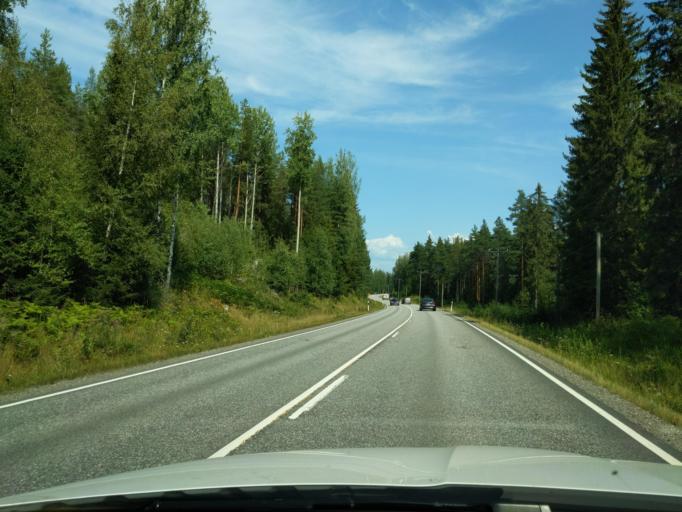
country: FI
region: Paijanne Tavastia
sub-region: Lahti
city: Padasjoki
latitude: 61.3320
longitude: 25.2146
